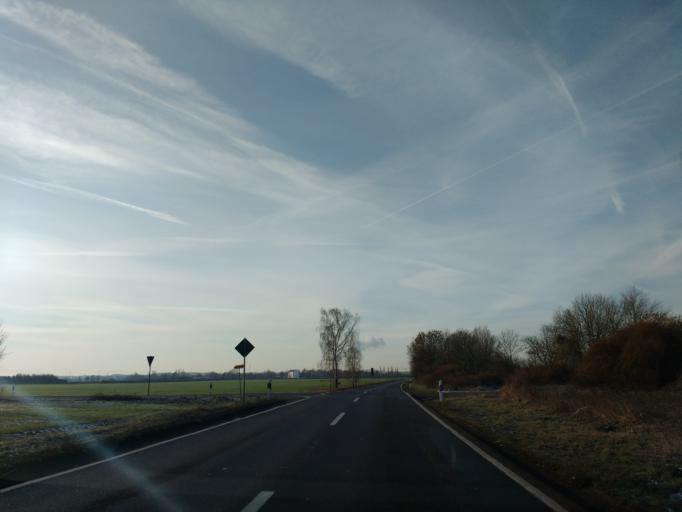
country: DE
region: Saxony-Anhalt
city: Oppin
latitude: 51.5385
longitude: 12.0111
